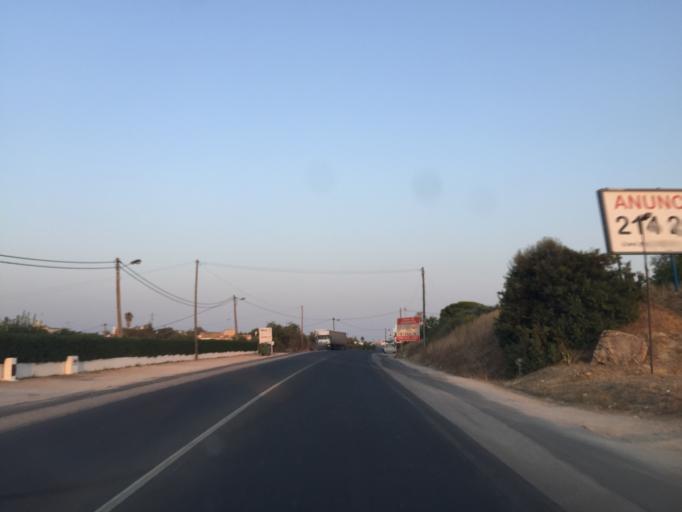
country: PT
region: Faro
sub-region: Faro
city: Santa Barbara de Nexe
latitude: 37.0791
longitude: -7.9927
